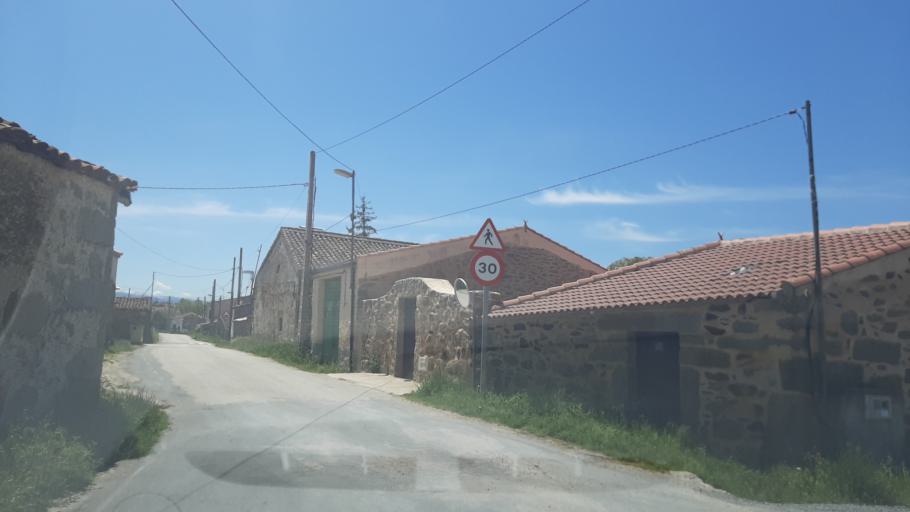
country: ES
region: Castille and Leon
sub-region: Provincia de Avila
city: Narrillos del Alamo
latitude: 40.5395
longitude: -5.4496
